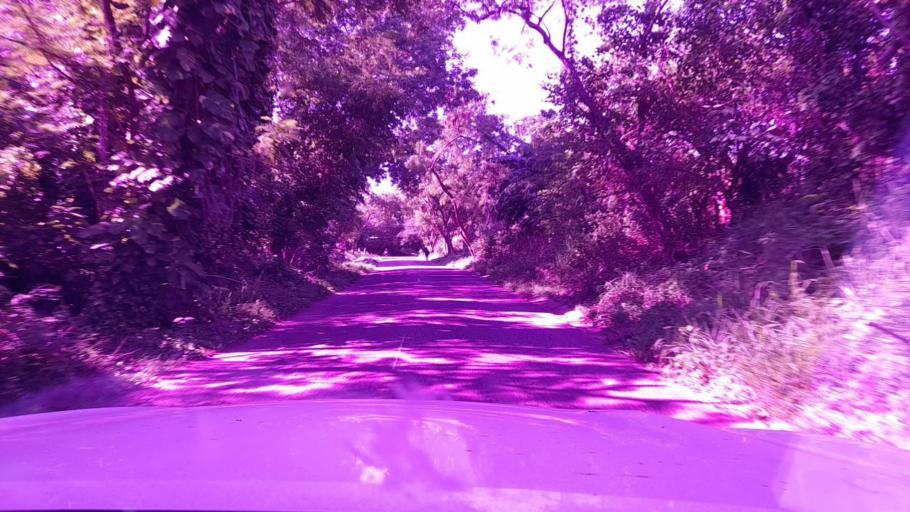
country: CU
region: La Habana
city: Alamar
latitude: 23.1632
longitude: -82.2761
